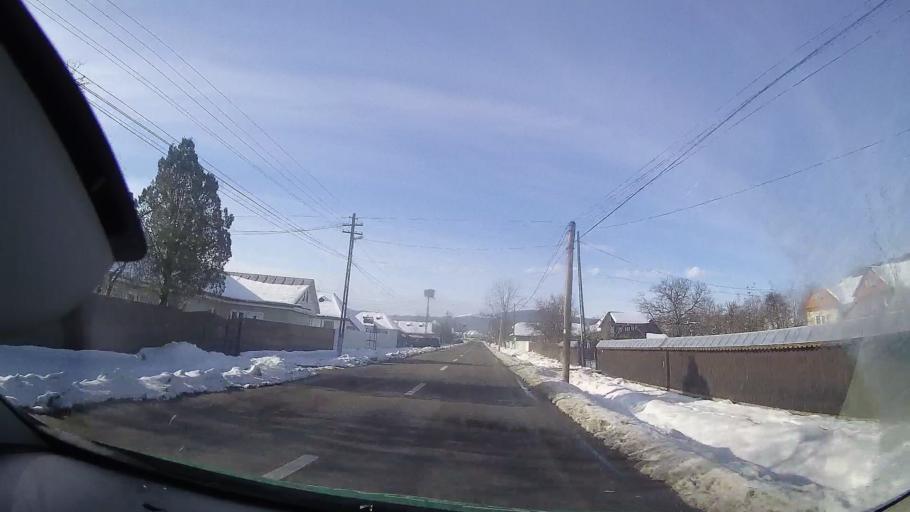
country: RO
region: Neamt
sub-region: Comuna Agapia
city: Agapia
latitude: 47.1738
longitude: 26.3051
